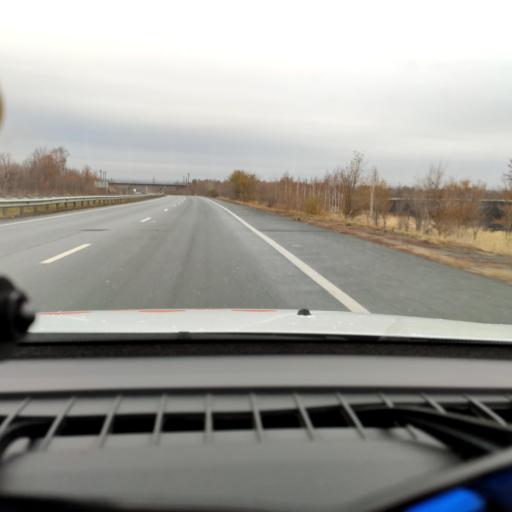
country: RU
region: Samara
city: Novokuybyshevsk
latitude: 53.0164
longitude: 49.9817
